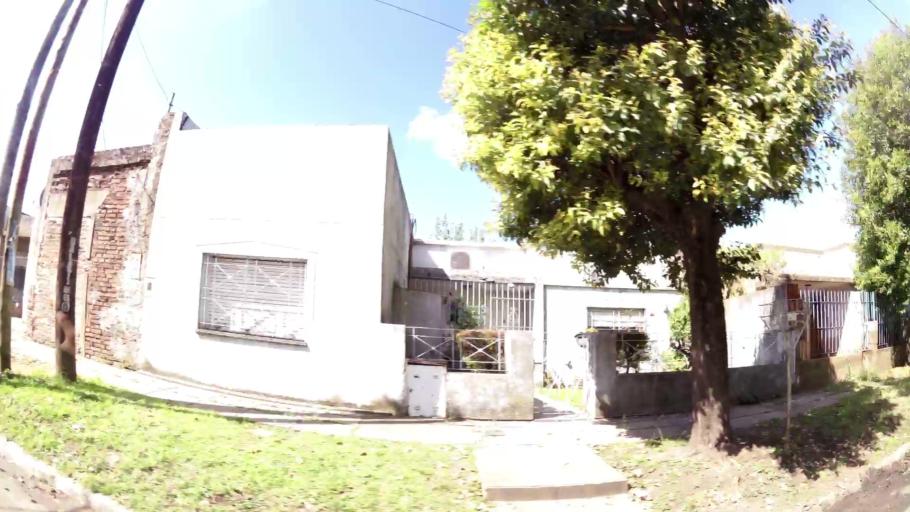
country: AR
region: Buenos Aires
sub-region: Partido de Quilmes
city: Quilmes
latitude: -34.8182
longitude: -58.2642
